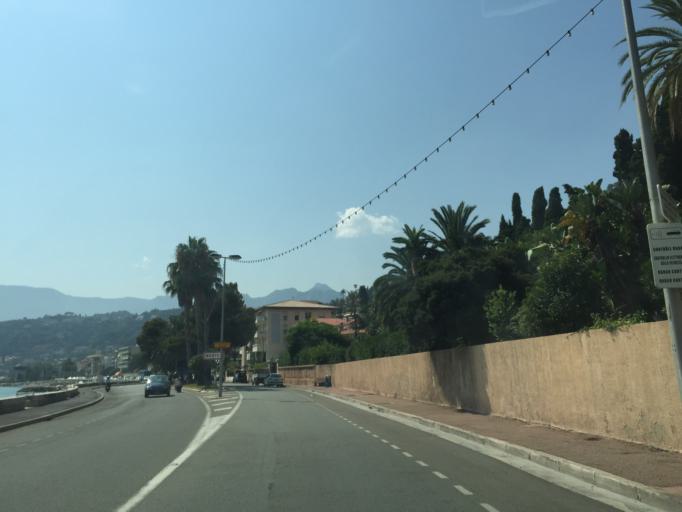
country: FR
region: Provence-Alpes-Cote d'Azur
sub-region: Departement des Alpes-Maritimes
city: Menton
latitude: 43.7850
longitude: 7.5278
